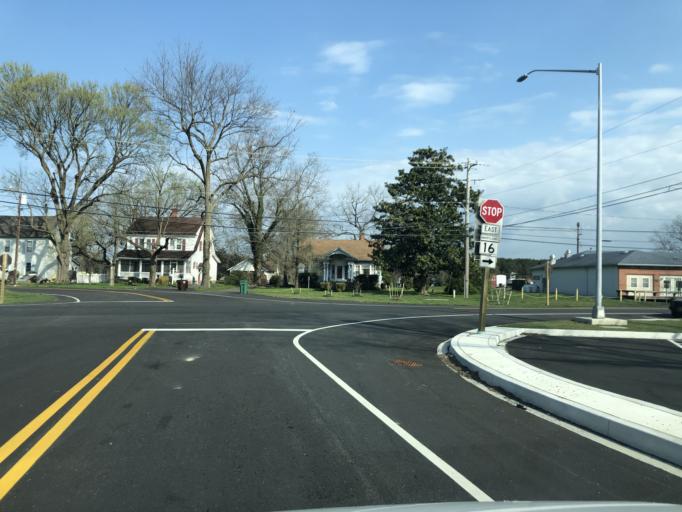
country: US
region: Maryland
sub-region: Dorchester County
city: Algonquin
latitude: 38.5019
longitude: -76.1524
